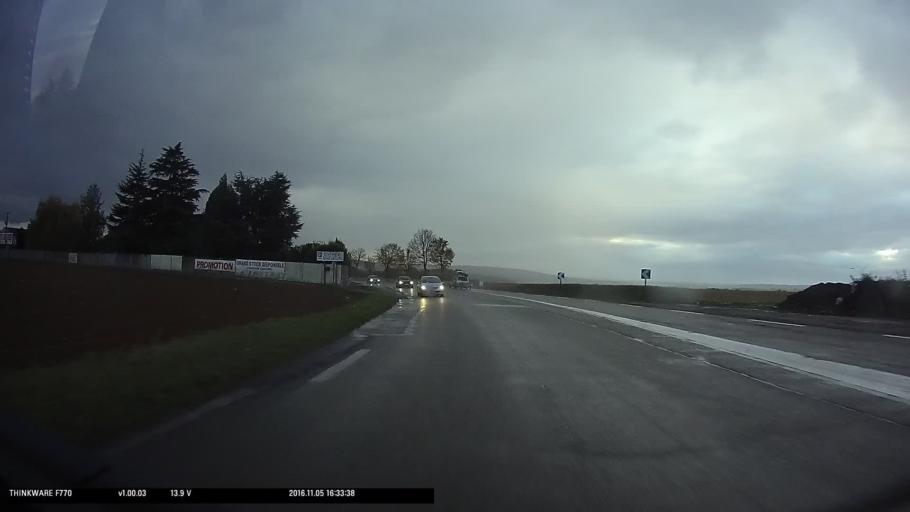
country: FR
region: Ile-de-France
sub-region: Departement du Val-d'Oise
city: Sagy
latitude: 49.0662
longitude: 1.9614
